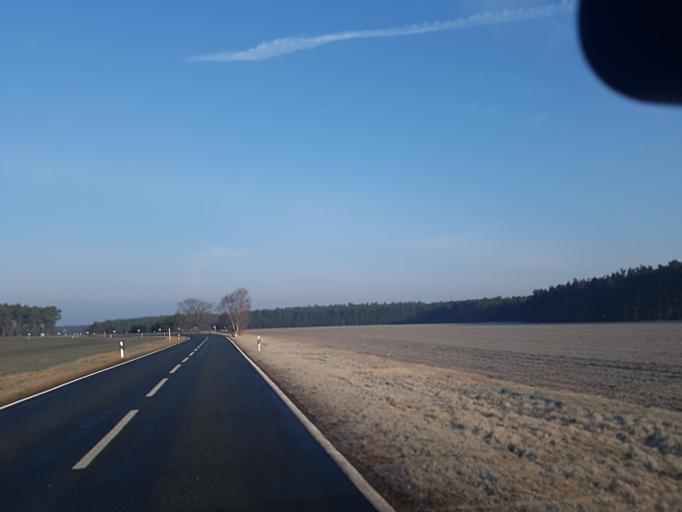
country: DE
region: Brandenburg
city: Golzow
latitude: 52.2521
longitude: 12.6906
